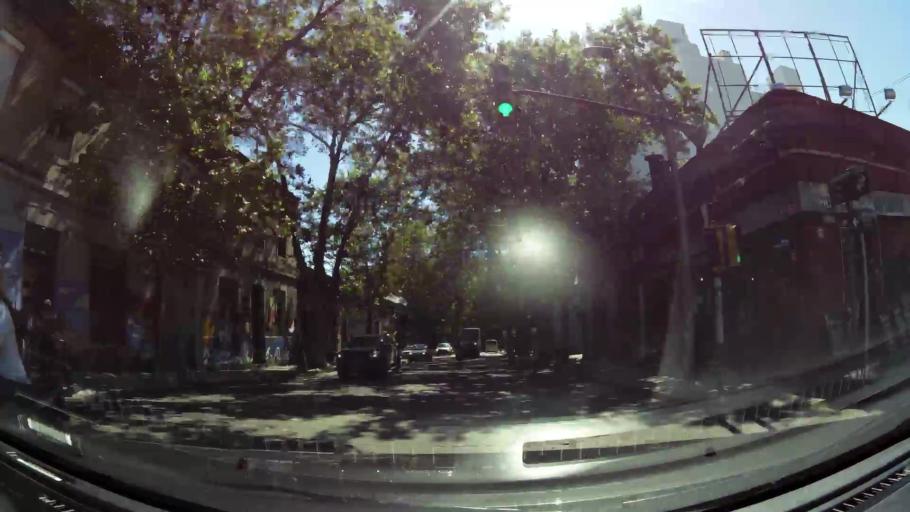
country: UY
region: Montevideo
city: Montevideo
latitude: -34.9029
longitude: -56.1462
